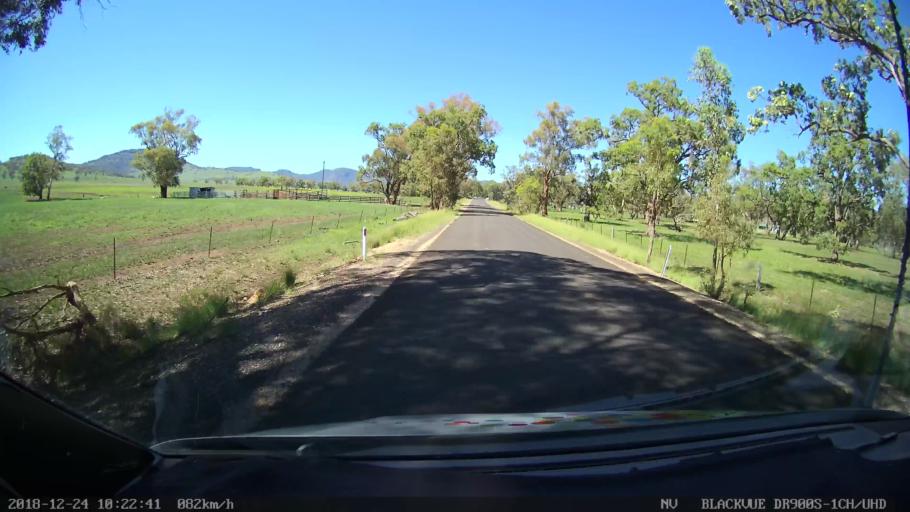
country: AU
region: New South Wales
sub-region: Liverpool Plains
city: Quirindi
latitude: -31.7672
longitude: 150.5428
